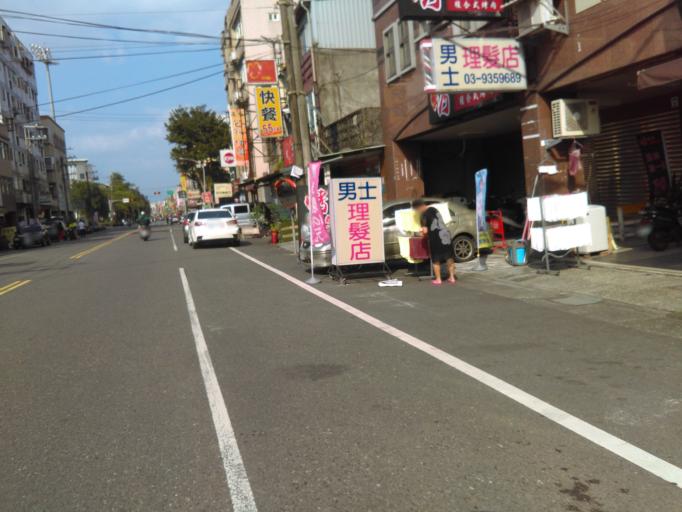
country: TW
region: Taiwan
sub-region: Yilan
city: Yilan
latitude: 24.7438
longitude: 121.7479
